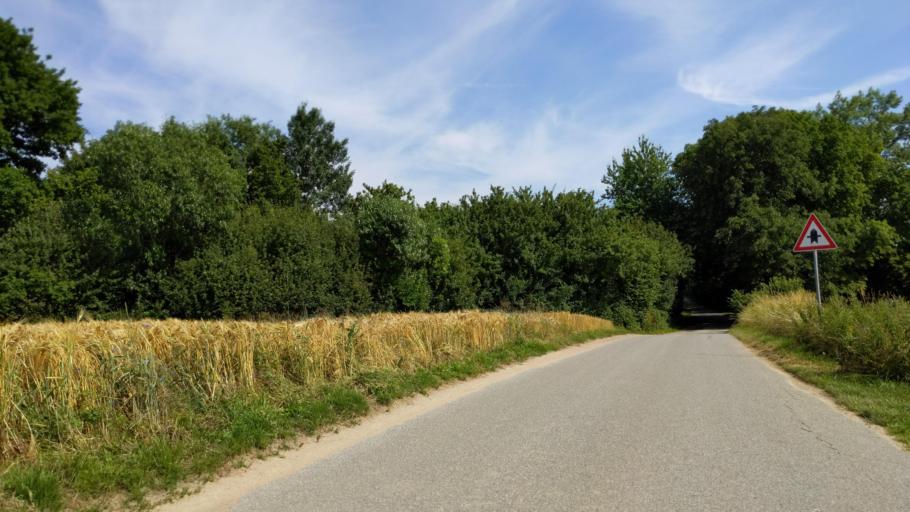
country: DE
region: Schleswig-Holstein
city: Eutin
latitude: 54.1085
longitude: 10.5965
